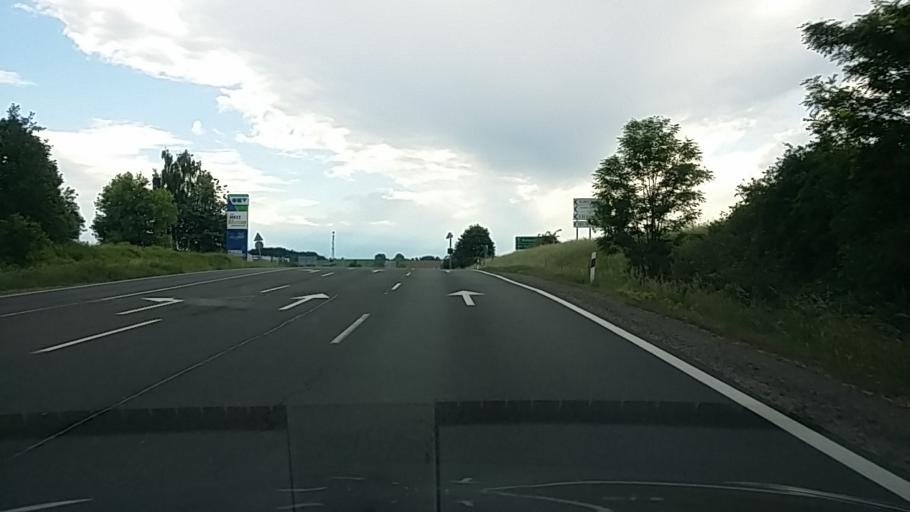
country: HU
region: Nograd
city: Retsag
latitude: 47.9205
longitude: 19.1220
